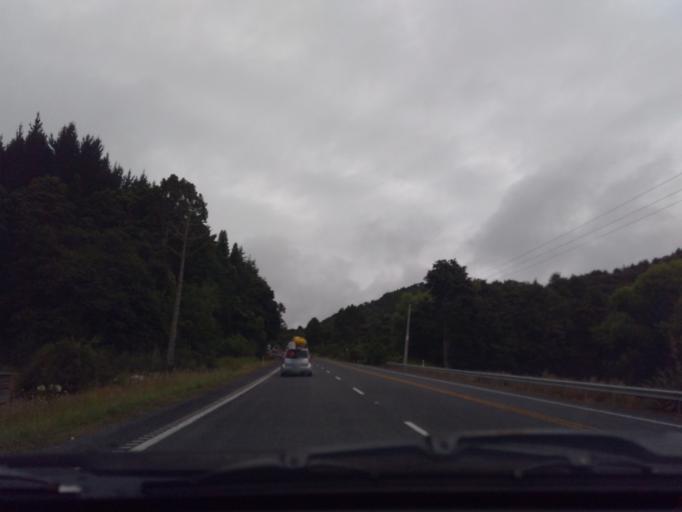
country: NZ
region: Auckland
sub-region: Auckland
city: Wellsford
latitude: -36.1200
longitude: 174.4359
